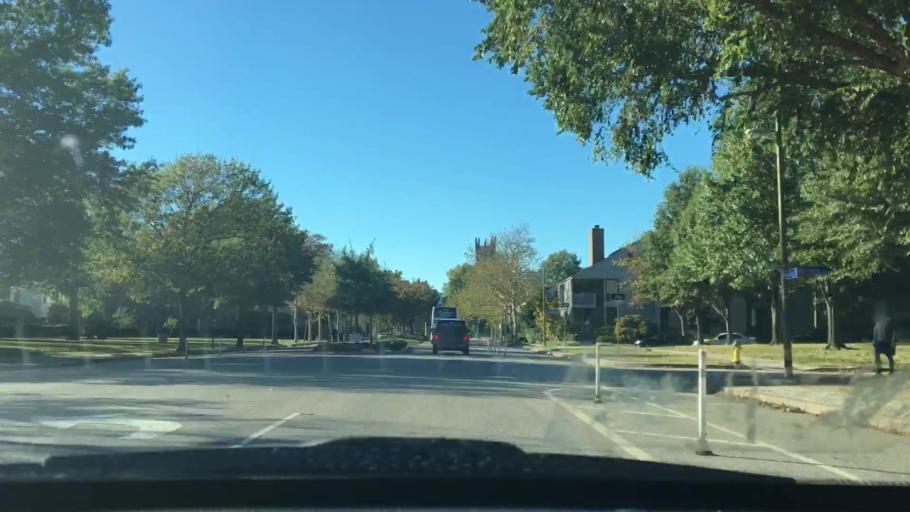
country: US
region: Virginia
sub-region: City of Norfolk
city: Norfolk
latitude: 36.8581
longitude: -76.2948
